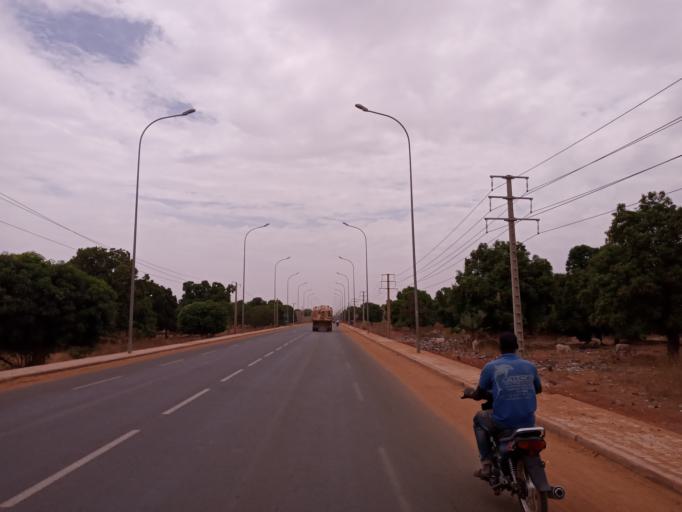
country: ML
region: Koulikoro
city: Koulikoro
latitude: 12.8490
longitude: -7.5749
